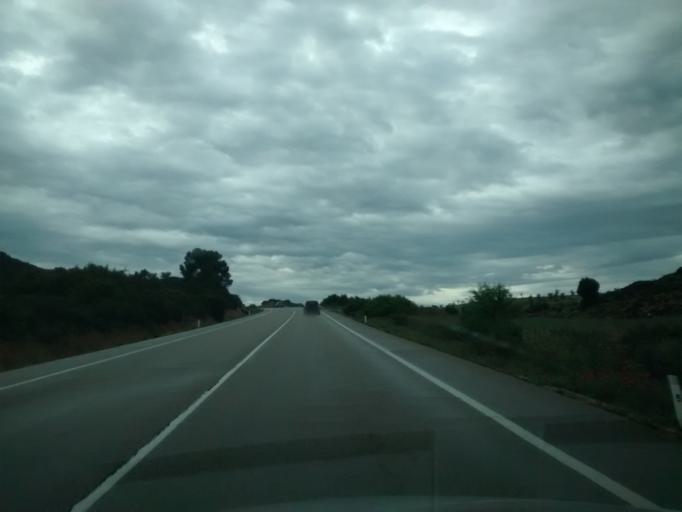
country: ES
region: Aragon
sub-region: Provincia de Zaragoza
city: Maella
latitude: 41.1406
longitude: 0.1197
